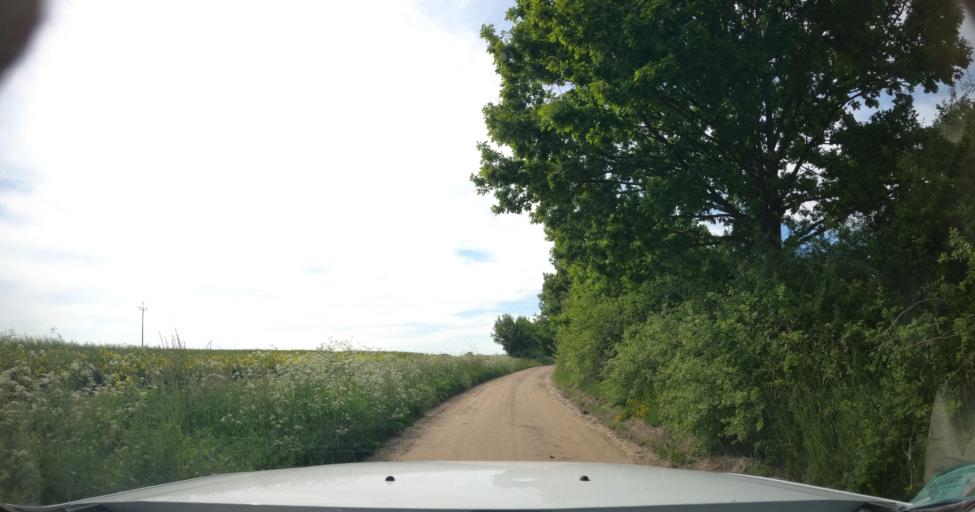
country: PL
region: Warmian-Masurian Voivodeship
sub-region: Powiat ostrodzki
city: Milakowo
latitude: 54.0154
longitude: 20.0114
